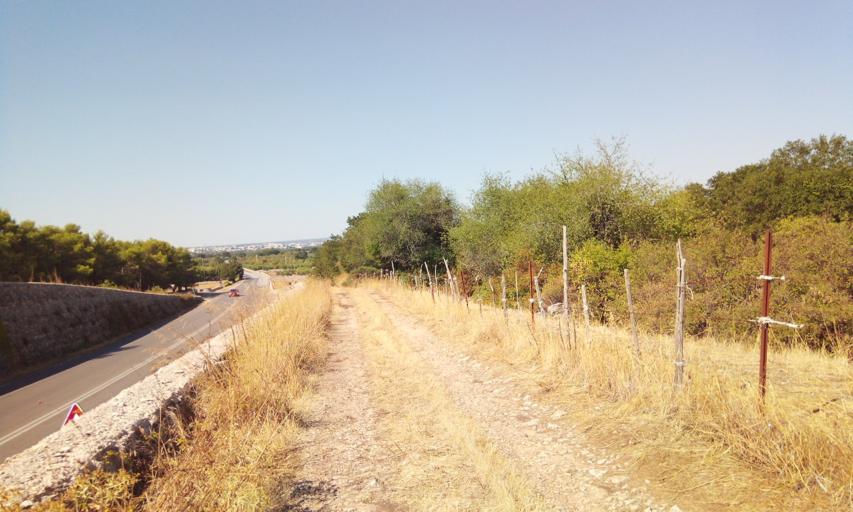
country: IT
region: Apulia
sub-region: Provincia di Bari
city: Gioia del Colle
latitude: 40.8295
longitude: 16.9708
